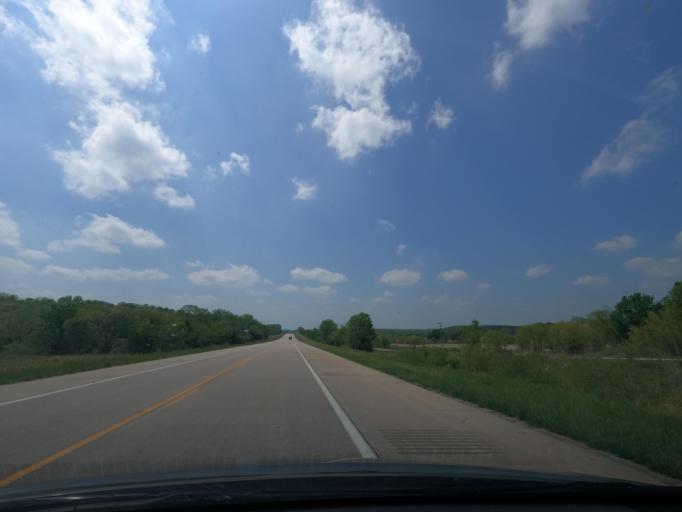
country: US
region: Kansas
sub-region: Wilson County
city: Fredonia
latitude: 37.6183
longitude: -95.9602
